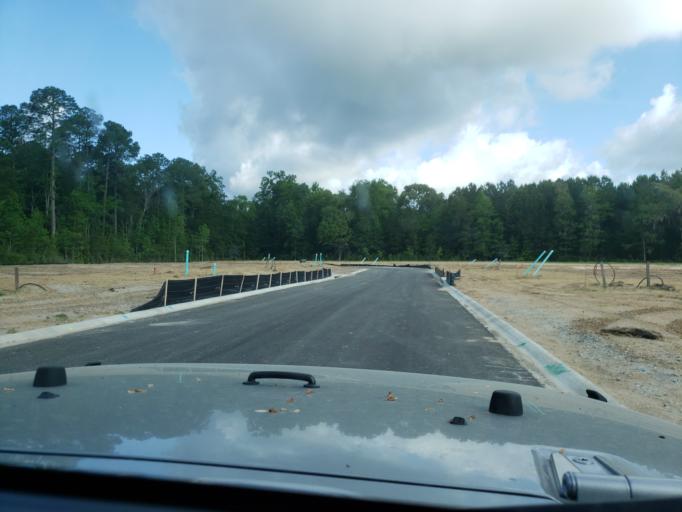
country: US
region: Georgia
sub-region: Chatham County
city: Georgetown
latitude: 32.0431
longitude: -81.2272
